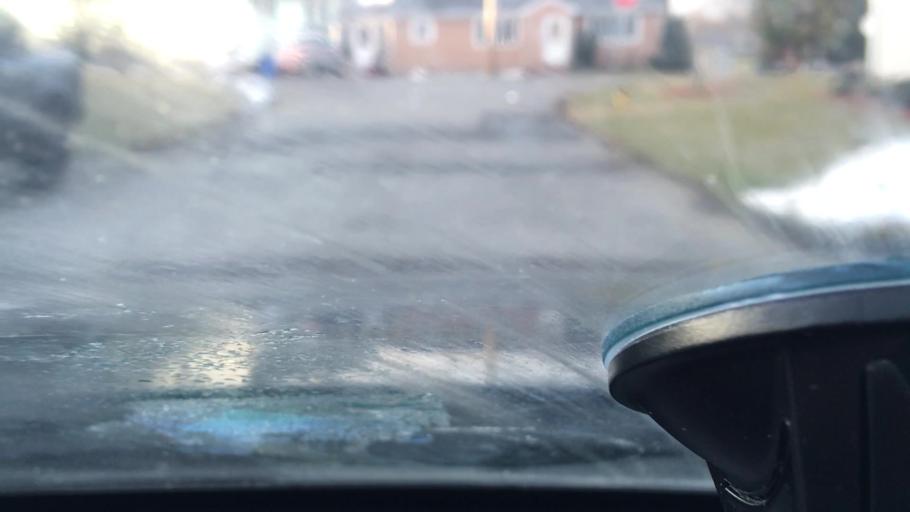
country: US
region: Massachusetts
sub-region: Middlesex County
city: Watertown
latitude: 42.3820
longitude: -71.2013
